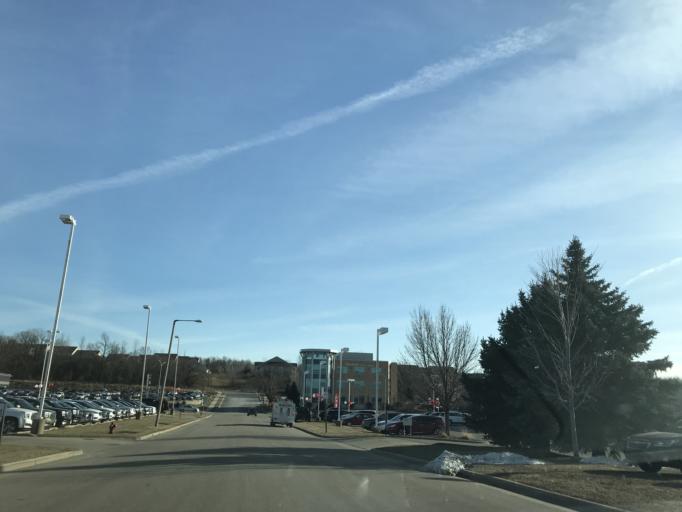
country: US
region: Wisconsin
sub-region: Dane County
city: Sun Prairie
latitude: 43.1414
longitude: -89.2883
